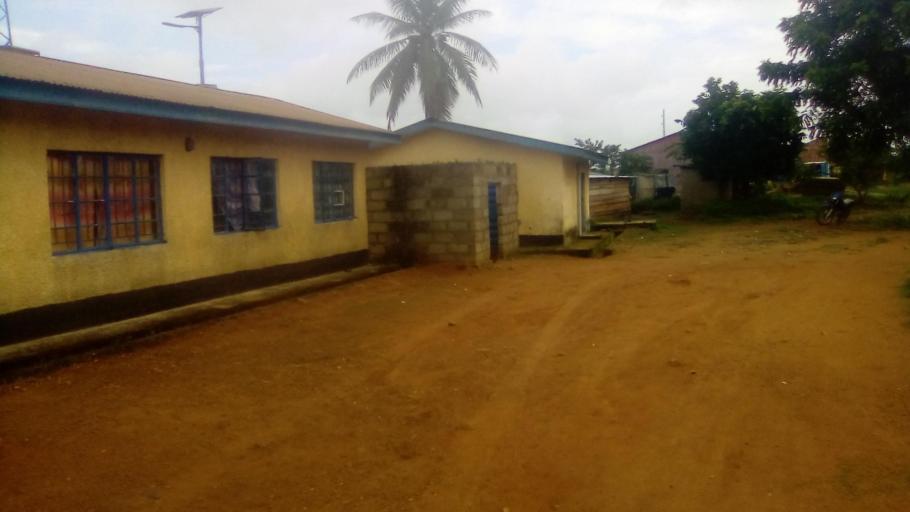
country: SL
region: Eastern Province
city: Kailahun
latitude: 8.2757
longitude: -10.5729
